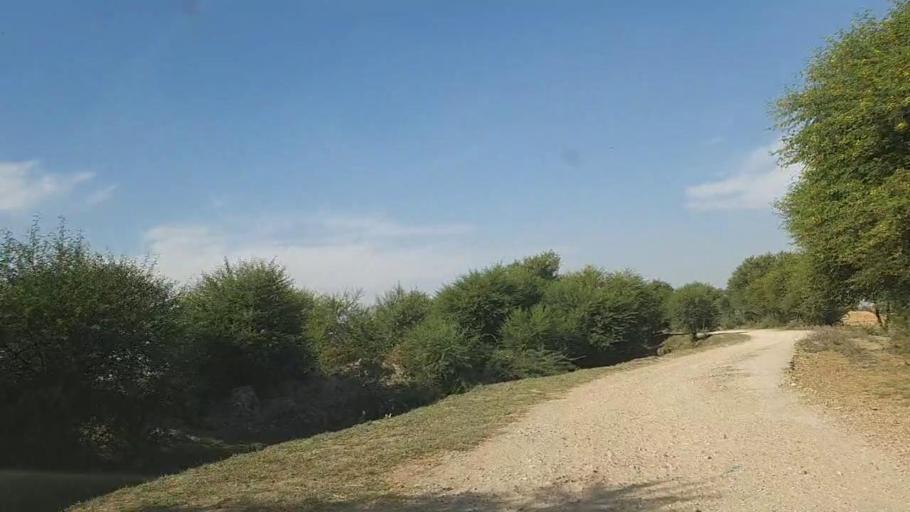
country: PK
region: Sindh
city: Bulri
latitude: 24.8653
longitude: 68.2672
